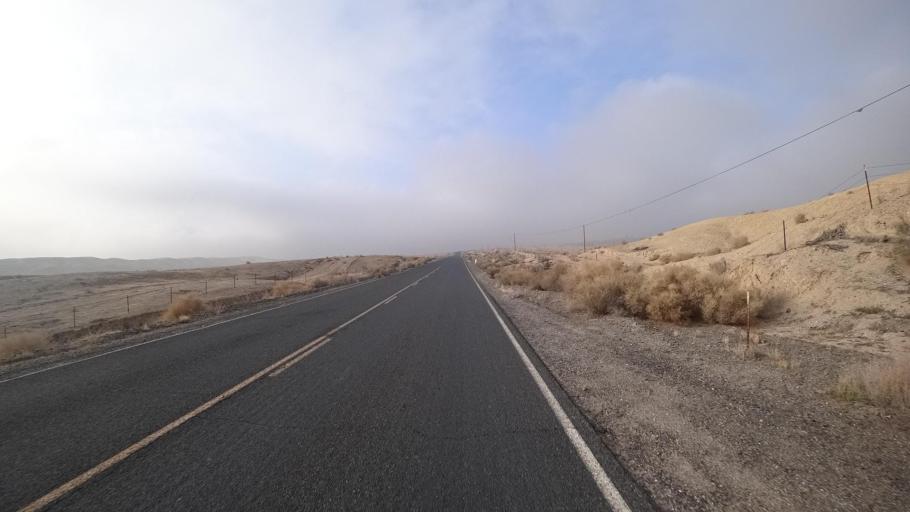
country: US
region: California
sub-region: Kern County
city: Ford City
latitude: 35.2428
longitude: -119.4549
